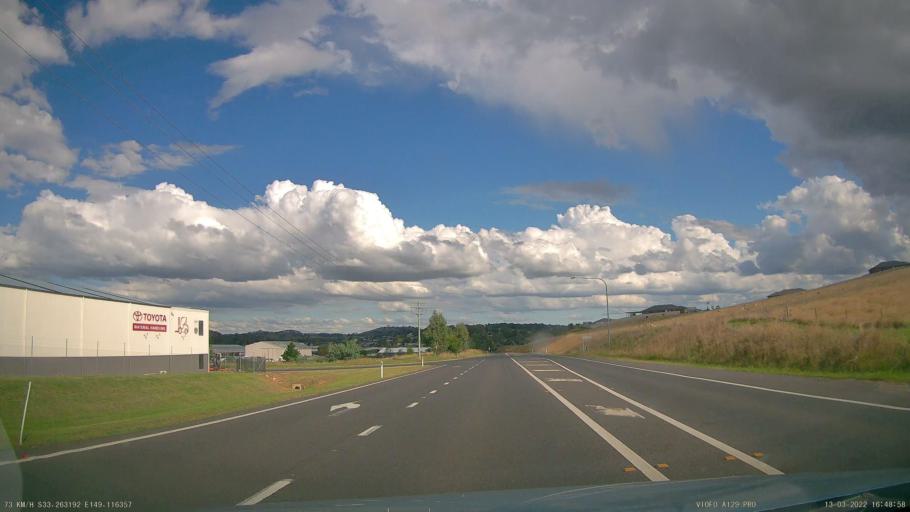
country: AU
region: New South Wales
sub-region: Orange Municipality
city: Orange
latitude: -33.2632
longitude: 149.1164
